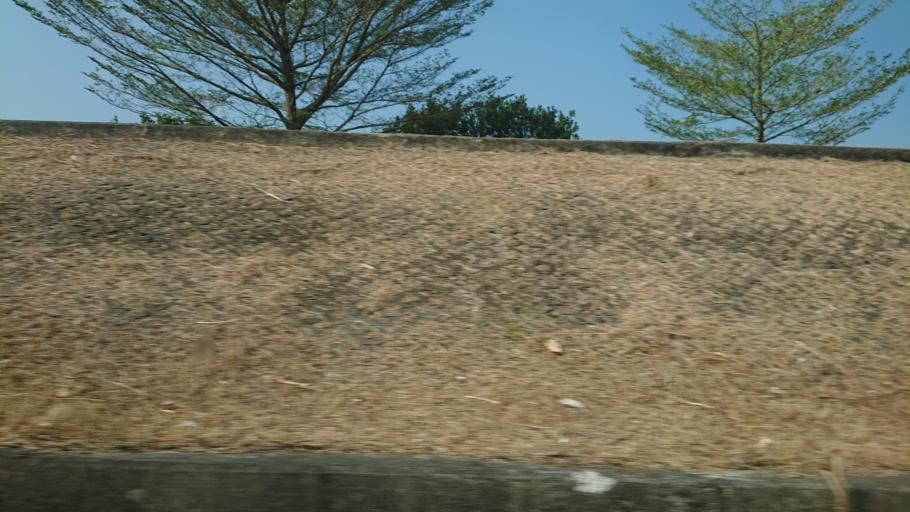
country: TW
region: Taiwan
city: Lugu
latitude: 23.7559
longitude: 120.6590
